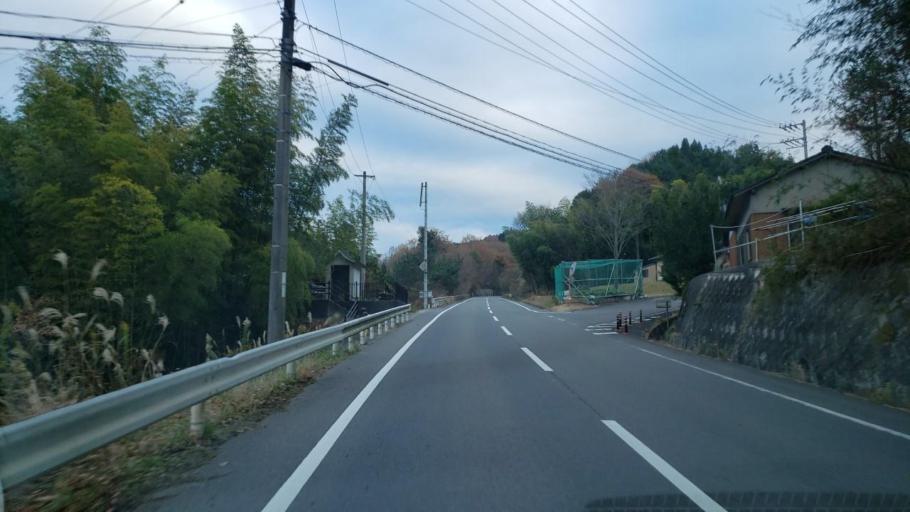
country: JP
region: Tokushima
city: Wakimachi
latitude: 34.1830
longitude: 134.1770
